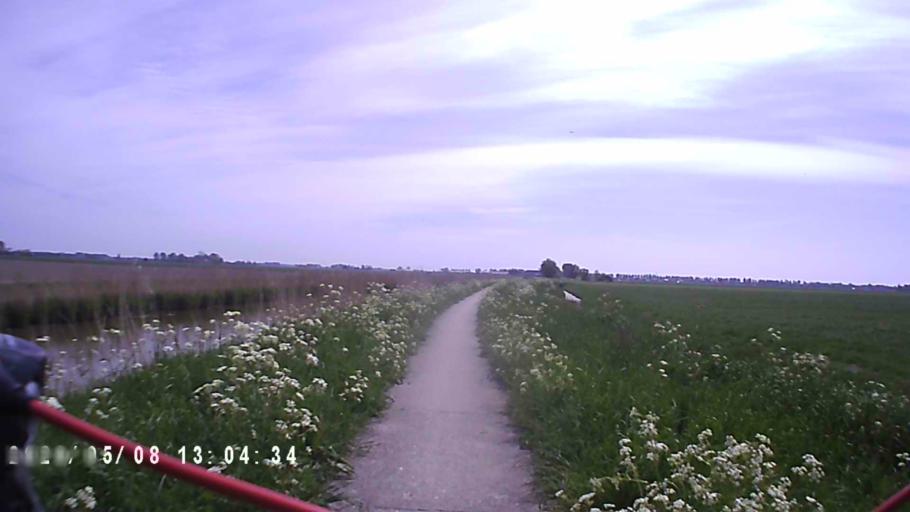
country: NL
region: Groningen
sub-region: Gemeente Bedum
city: Bedum
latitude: 53.2973
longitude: 6.6898
